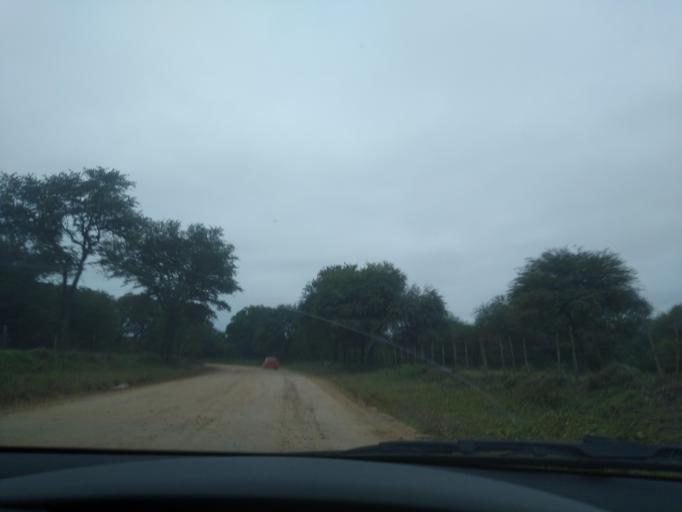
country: AR
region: Chaco
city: Colonia Benitez
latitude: -27.3424
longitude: -58.9692
